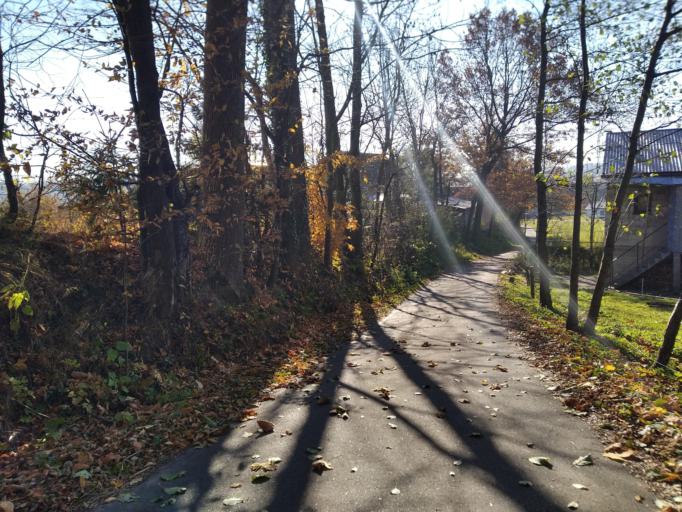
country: PL
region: Subcarpathian Voivodeship
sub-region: Powiat strzyzowski
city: Frysztak
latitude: 49.8522
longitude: 21.6119
